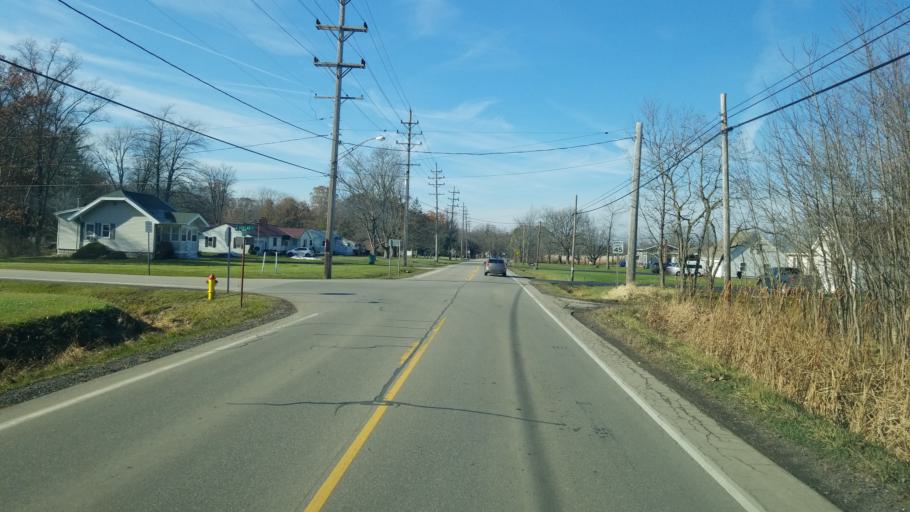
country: US
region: Ohio
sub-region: Ashtabula County
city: Jefferson
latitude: 41.7464
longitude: -80.7793
